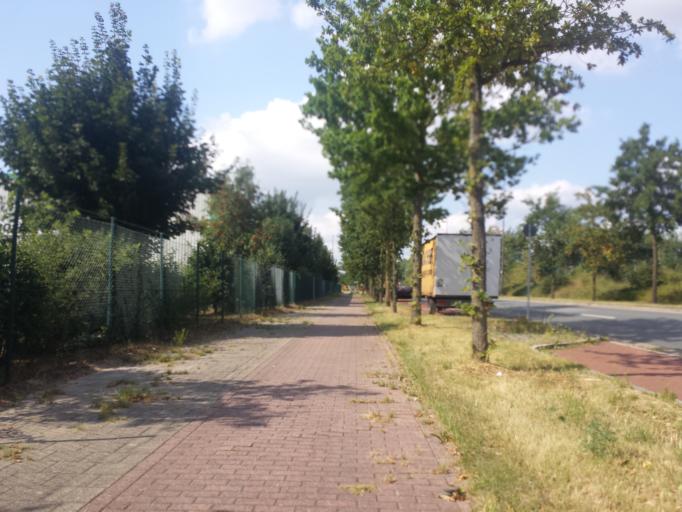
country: DE
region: Lower Saxony
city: Stuhr
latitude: 53.0929
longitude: 8.7111
